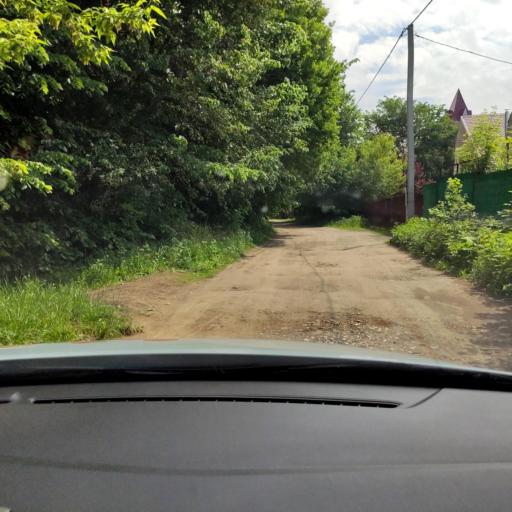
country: RU
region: Tatarstan
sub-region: Gorod Kazan'
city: Kazan
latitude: 55.7012
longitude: 49.0890
